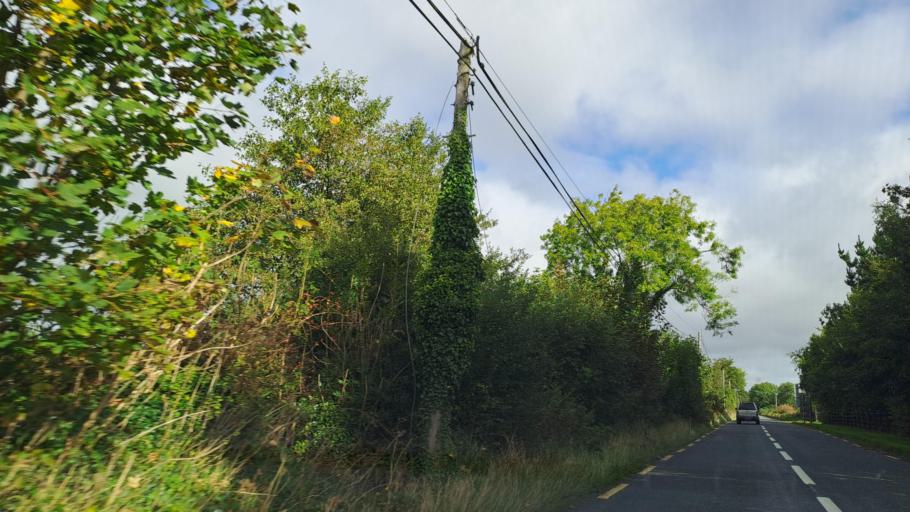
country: IE
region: Ulster
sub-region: An Cabhan
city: Kingscourt
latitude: 53.9212
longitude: -6.7846
